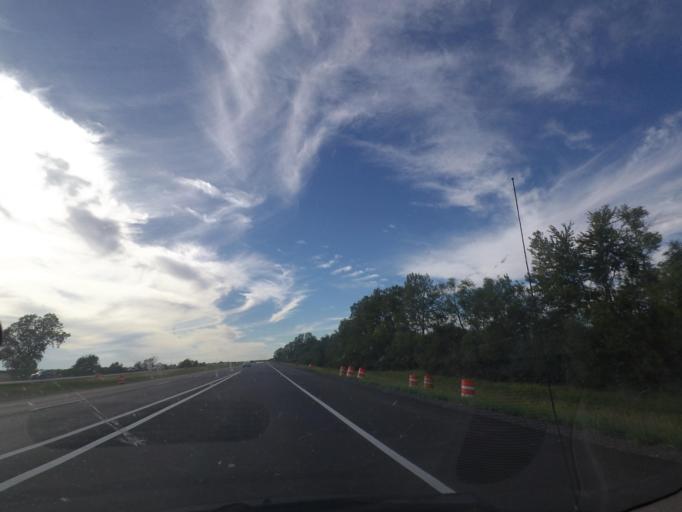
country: US
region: Illinois
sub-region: Macon County
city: Harristown
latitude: 39.8362
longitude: -89.1605
